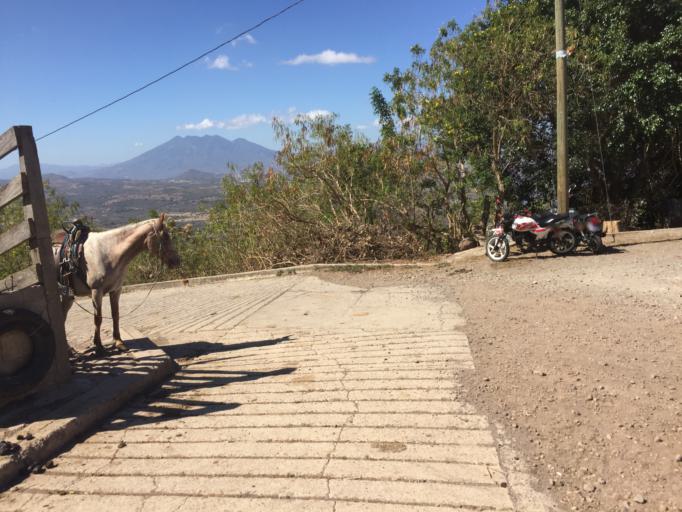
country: GT
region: Jutiapa
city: Agua Blanca
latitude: 14.5520
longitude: -89.6534
